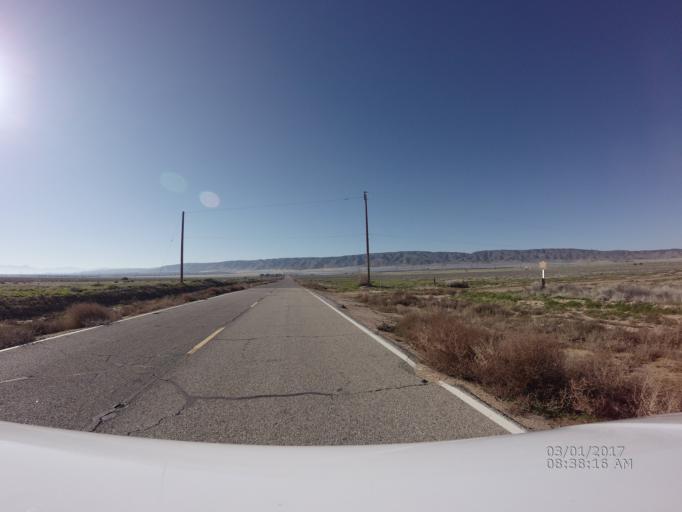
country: US
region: California
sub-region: Los Angeles County
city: Quartz Hill
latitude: 34.6823
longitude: -118.2716
